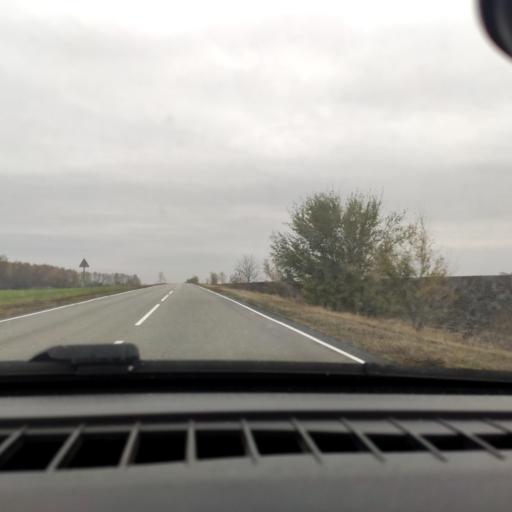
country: RU
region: Belgorod
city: Alekseyevka
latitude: 50.7659
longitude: 38.8424
